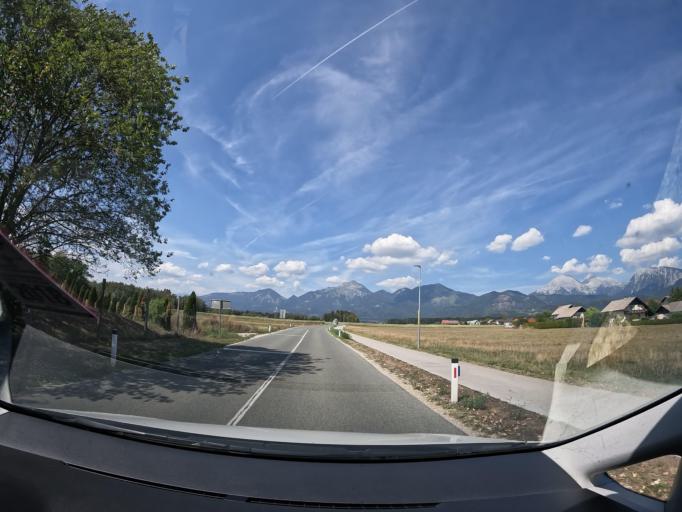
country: SI
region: Sencur
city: Sencur
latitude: 46.2519
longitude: 14.4200
